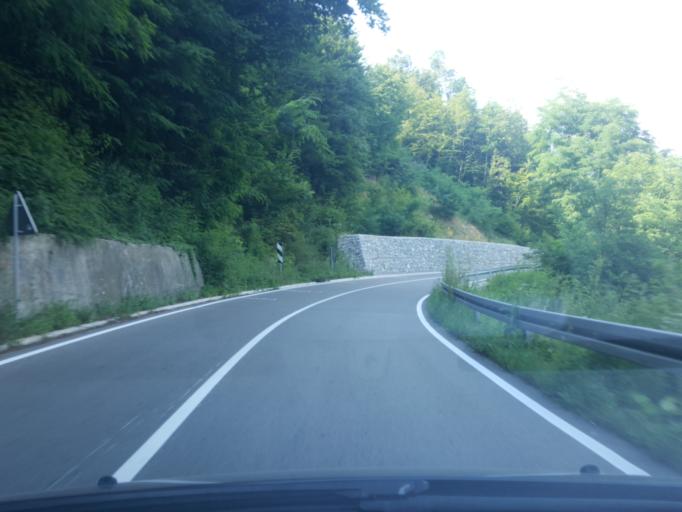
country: RS
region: Central Serbia
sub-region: Moravicki Okrug
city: Gornji Milanovac
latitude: 44.1532
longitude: 20.5054
